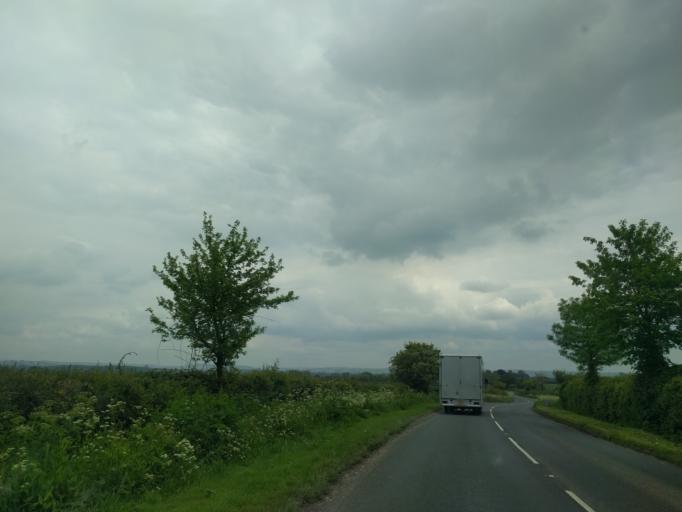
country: GB
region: England
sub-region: Somerset
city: Ilchester
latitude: 51.0765
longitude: -2.6322
